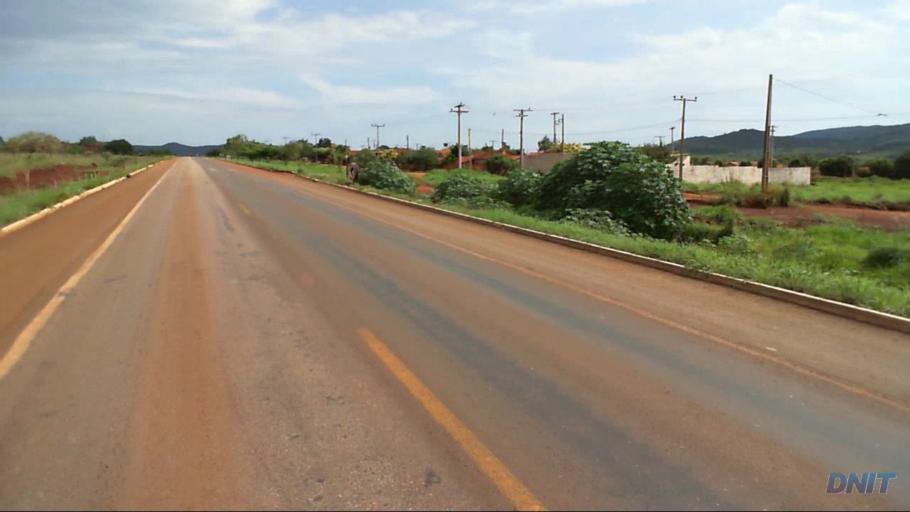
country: BR
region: Goias
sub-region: Barro Alto
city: Barro Alto
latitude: -14.9739
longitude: -48.9301
